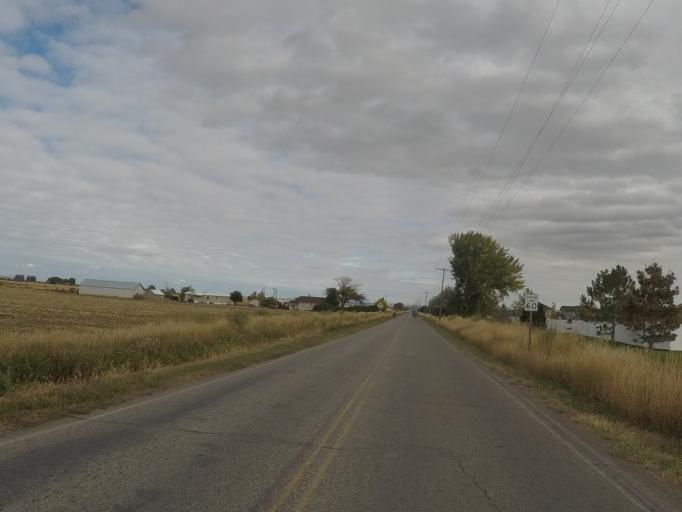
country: US
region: Montana
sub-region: Yellowstone County
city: Laurel
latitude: 45.7406
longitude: -108.6584
